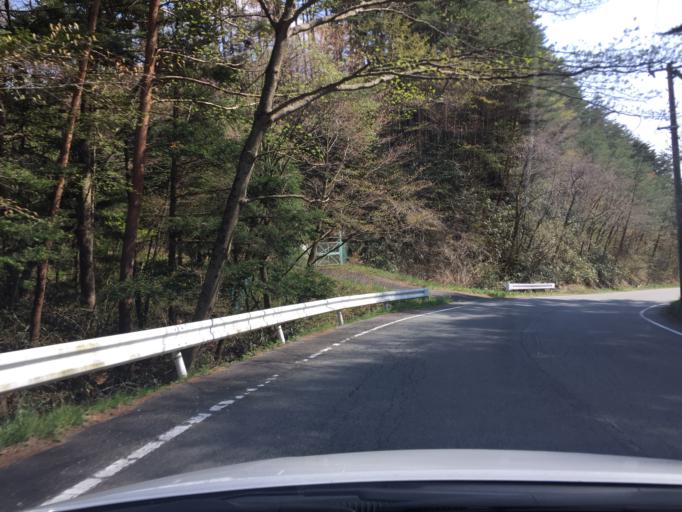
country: JP
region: Fukushima
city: Namie
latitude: 37.3815
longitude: 140.8011
